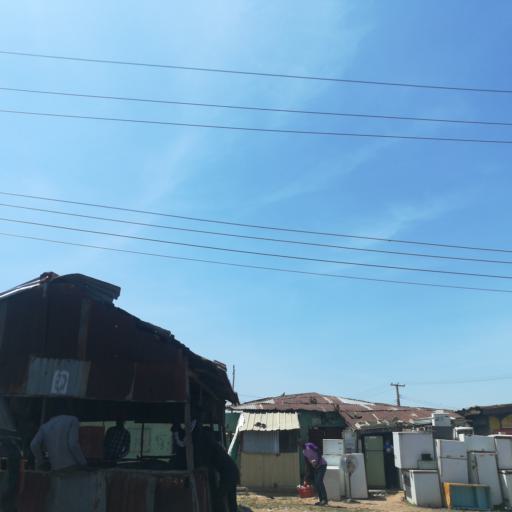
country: NG
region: Plateau
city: Bukuru
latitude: 9.8005
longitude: 8.8600
